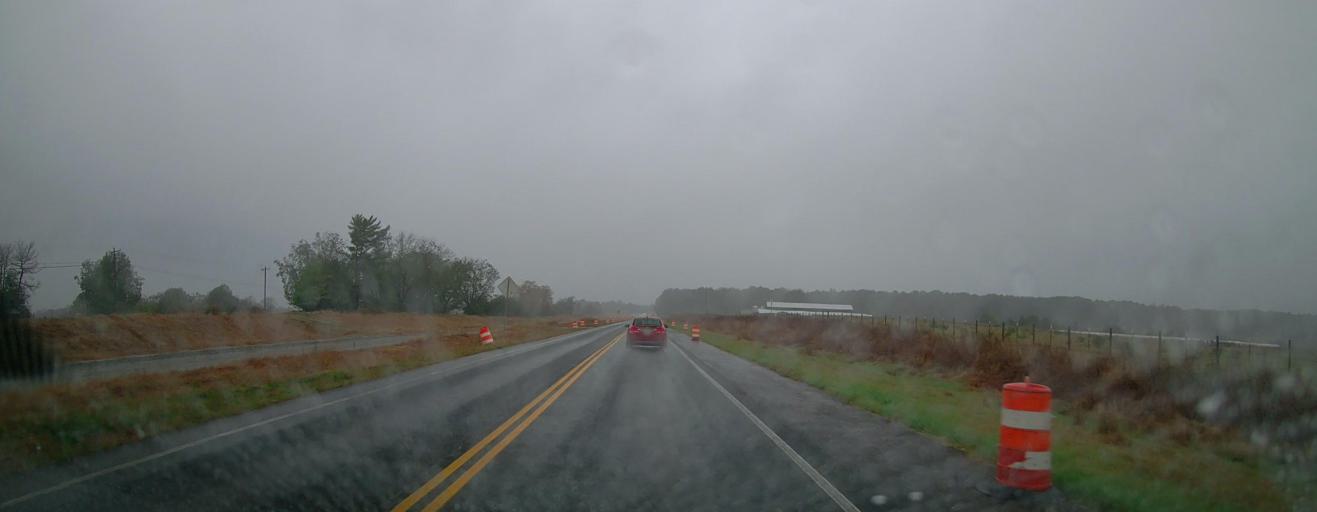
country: US
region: Georgia
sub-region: Putnam County
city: Jefferson
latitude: 33.4720
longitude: -83.4205
